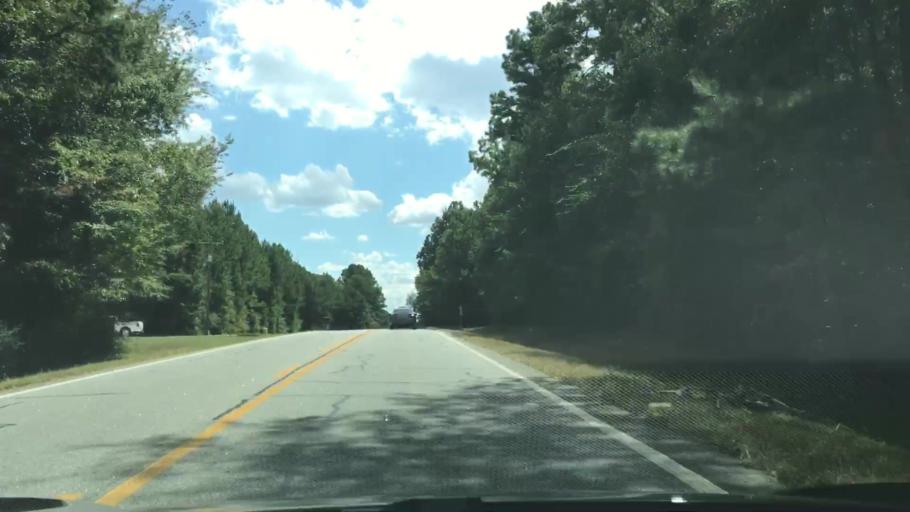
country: US
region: Georgia
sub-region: Oconee County
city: Watkinsville
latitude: 33.7711
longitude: -83.3103
